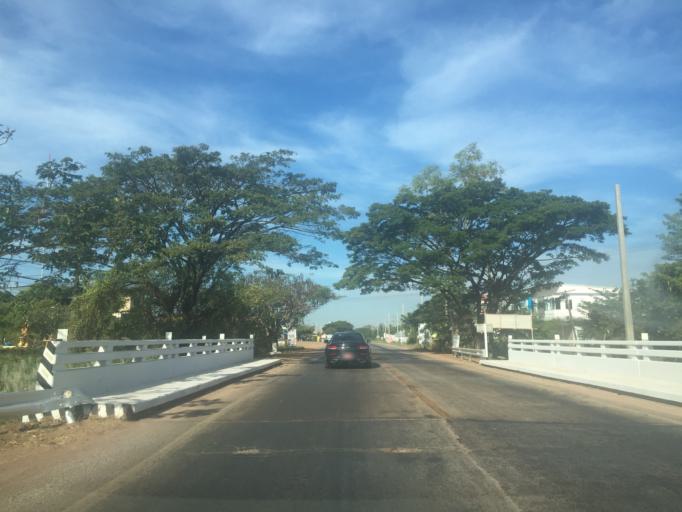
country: TH
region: Changwat Udon Thani
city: Kumphawapi
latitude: 17.1121
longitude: 103.0058
